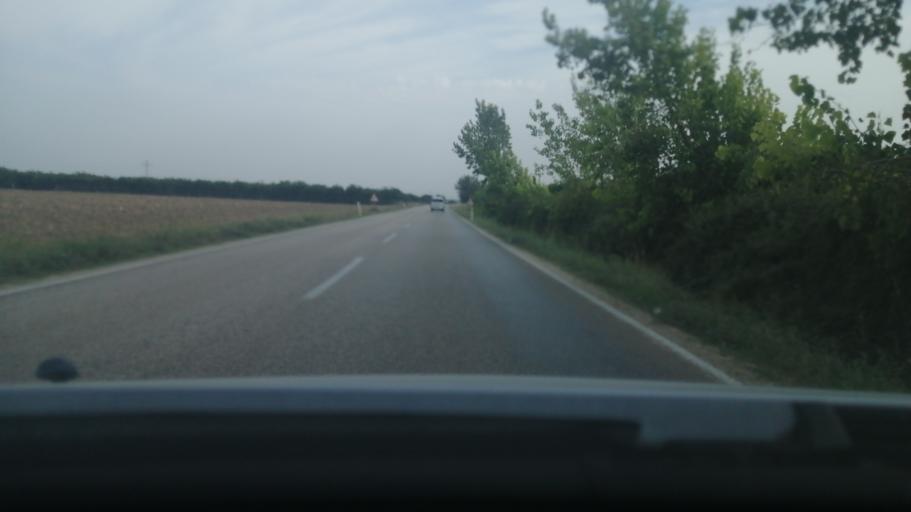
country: TR
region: Adana
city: Kozan
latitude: 37.3658
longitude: 35.8577
